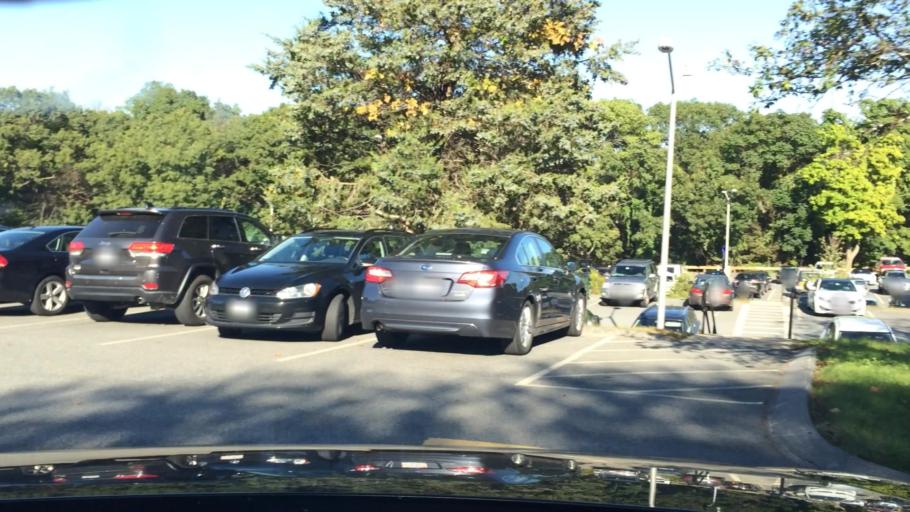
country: US
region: Massachusetts
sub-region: Middlesex County
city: Waltham
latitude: 42.3884
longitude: -71.2185
